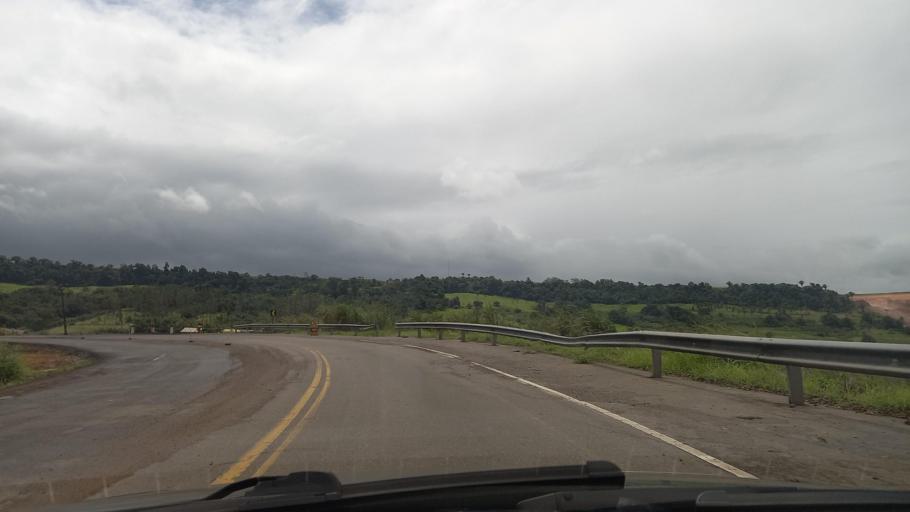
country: BR
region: Alagoas
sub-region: Sao Miguel Dos Campos
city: Sao Miguel dos Campos
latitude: -9.8195
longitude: -36.2194
